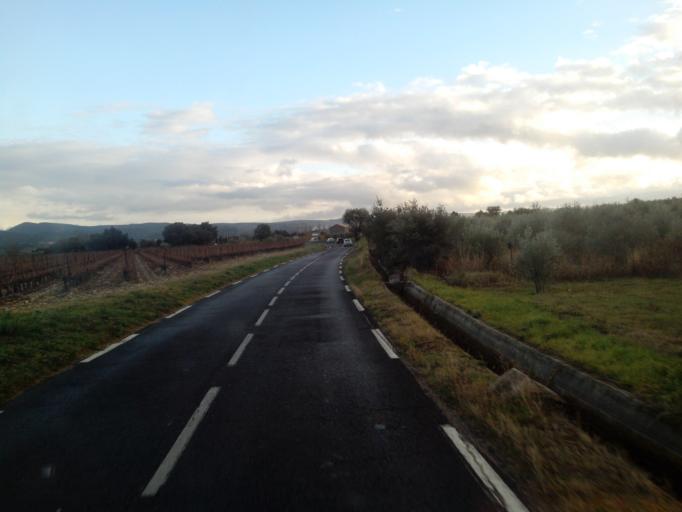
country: FR
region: Languedoc-Roussillon
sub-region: Departement de l'Herault
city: Saint-Jean-de-Fos
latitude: 43.7053
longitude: 3.5612
